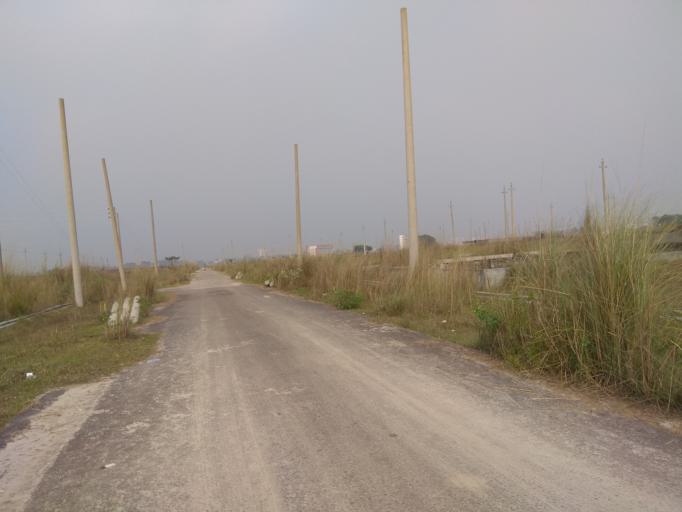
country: BD
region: Dhaka
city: Tungi
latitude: 23.8609
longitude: 90.3696
